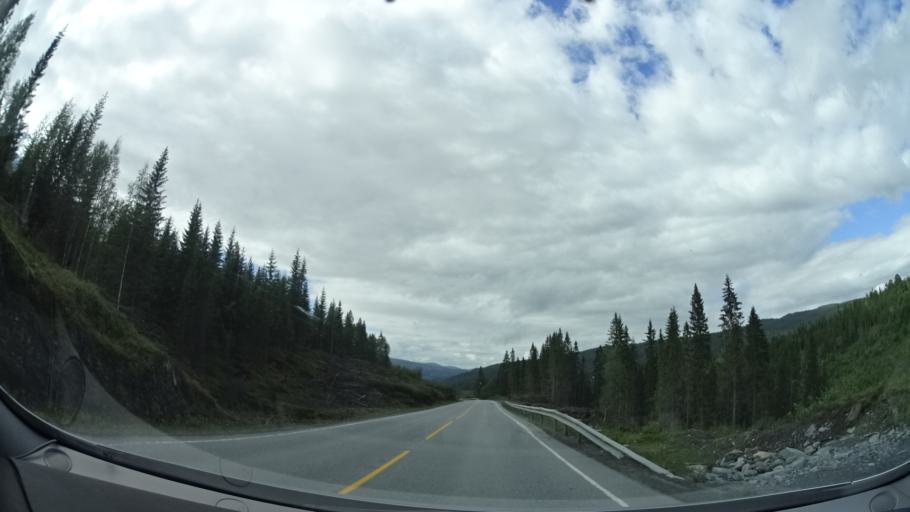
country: NO
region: Nord-Trondelag
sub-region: Meraker
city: Meraker
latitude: 63.3884
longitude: 11.8425
